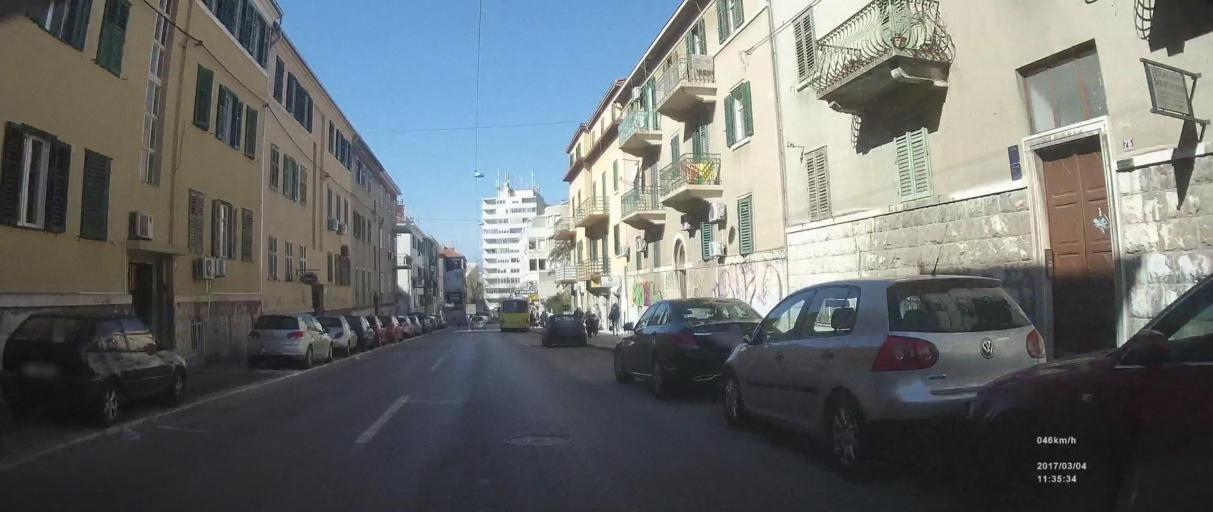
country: HR
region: Splitsko-Dalmatinska
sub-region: Grad Split
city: Split
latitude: 43.5055
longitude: 16.4511
